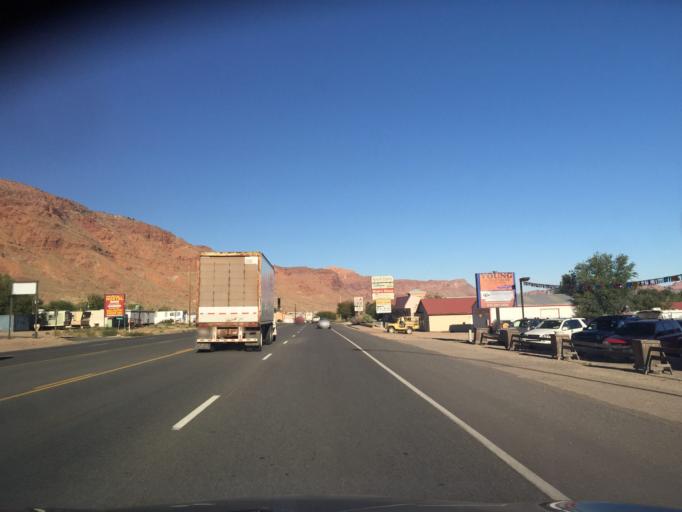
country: US
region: Utah
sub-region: Grand County
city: Moab
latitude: 38.5559
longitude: -109.5385
